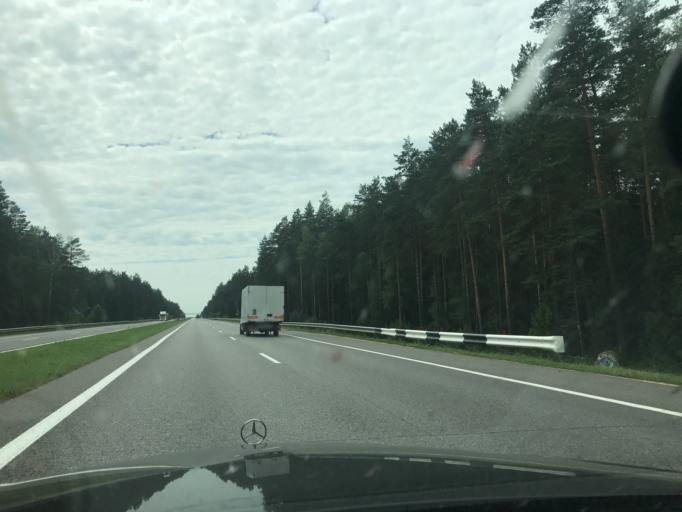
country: BY
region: Minsk
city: Slabada
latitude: 53.9107
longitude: 27.9504
